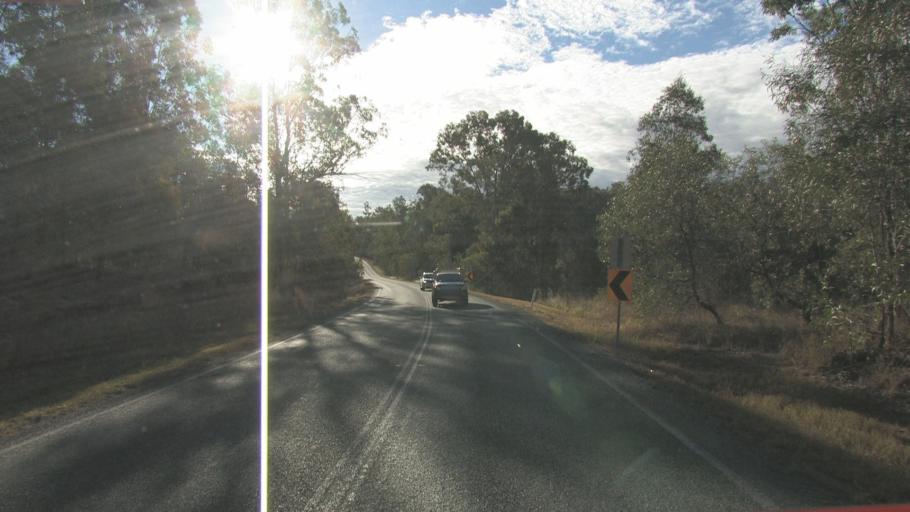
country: AU
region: Queensland
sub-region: Logan
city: Cedar Vale
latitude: -27.8939
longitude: 153.0875
